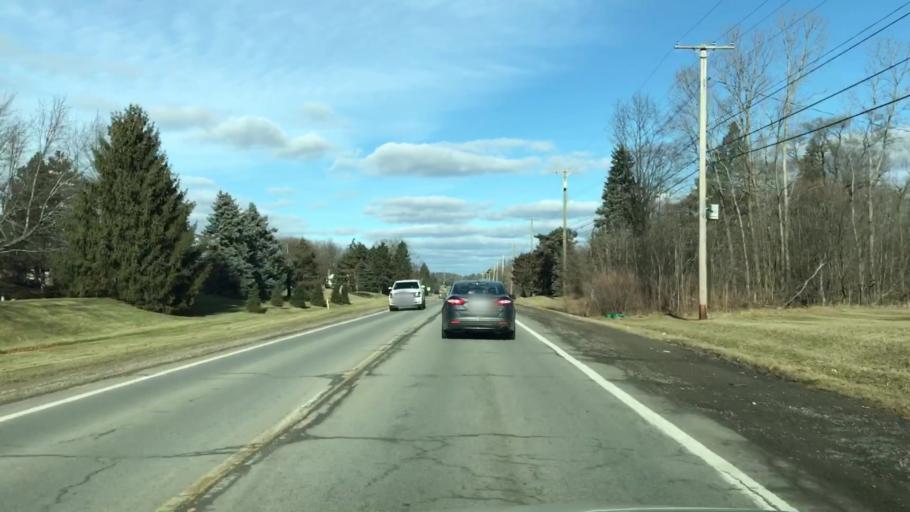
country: US
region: Michigan
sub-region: Oakland County
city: Auburn Hills
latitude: 42.6887
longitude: -83.1944
